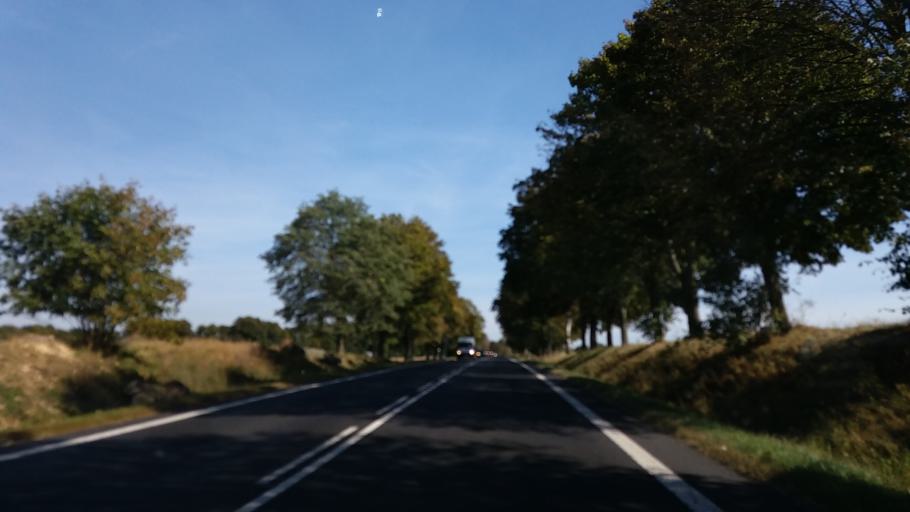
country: PL
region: Greater Poland Voivodeship
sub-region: Powiat miedzychodzki
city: Kwilcz
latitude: 52.5645
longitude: 16.0206
